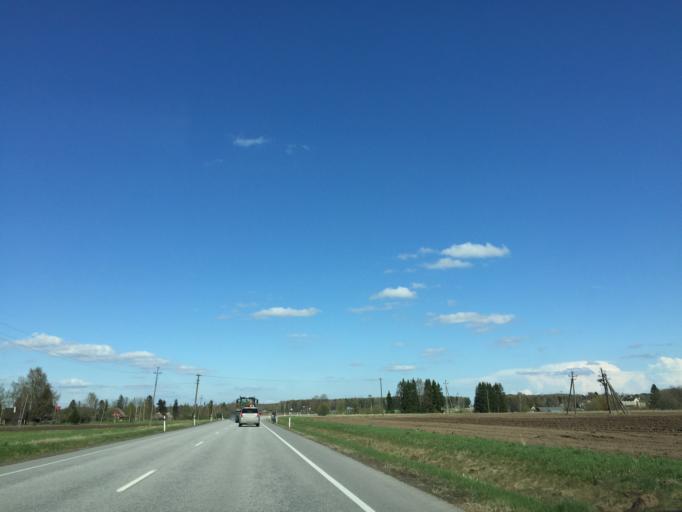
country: EE
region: Valgamaa
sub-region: Valga linn
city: Valga
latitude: 57.8690
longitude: 26.2362
